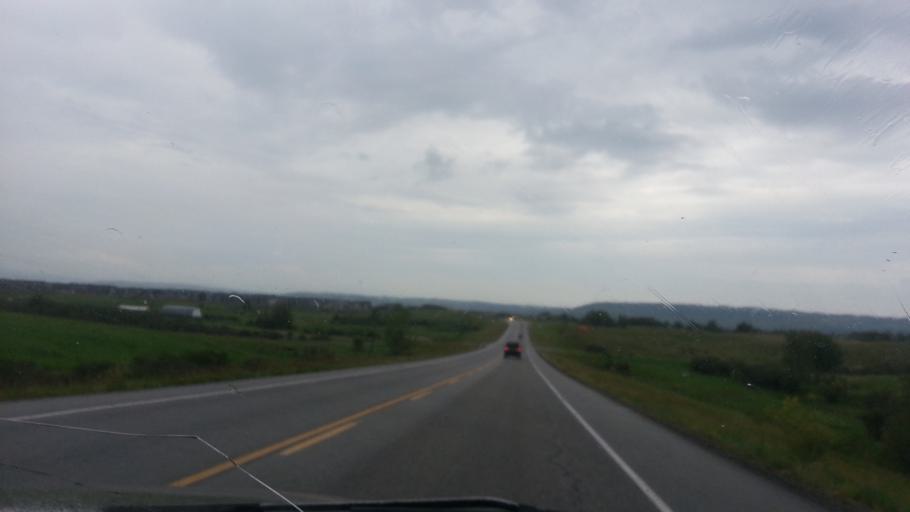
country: CA
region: Alberta
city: Cochrane
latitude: 51.1473
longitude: -114.4669
